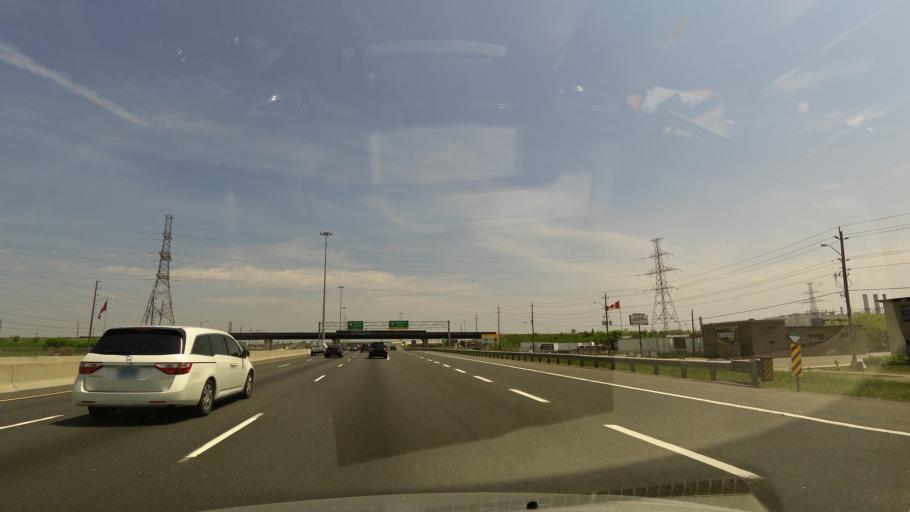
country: CA
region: Ontario
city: Oshawa
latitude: 43.8740
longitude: -78.8832
